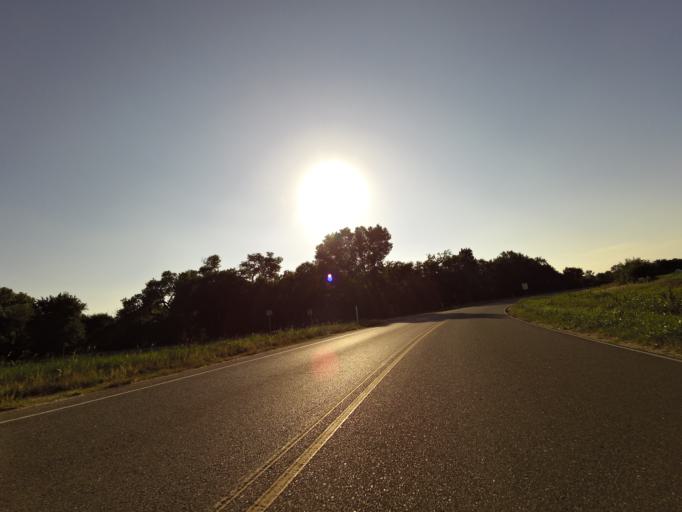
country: US
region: Kansas
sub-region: Reno County
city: Buhler
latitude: 38.1447
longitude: -97.8281
